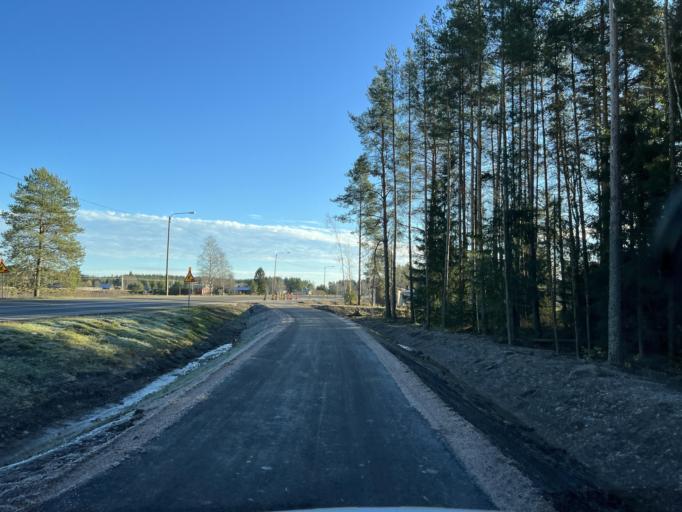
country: FI
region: Northern Ostrobothnia
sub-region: Nivala-Haapajaervi
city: Nivala
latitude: 63.9501
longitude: 24.9183
